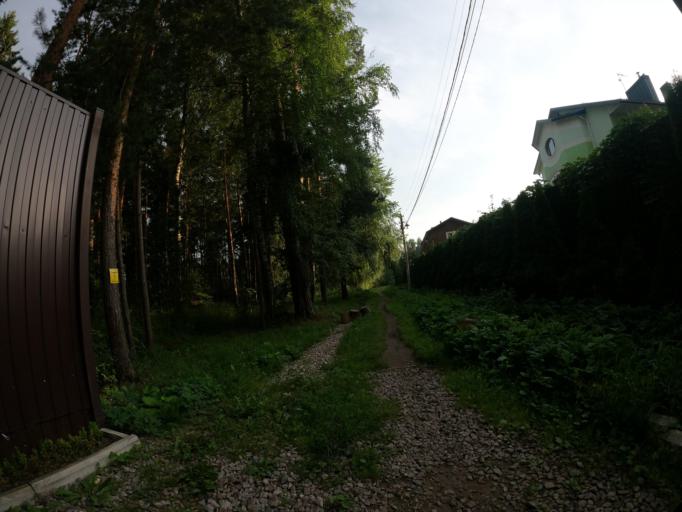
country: RU
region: Moskovskaya
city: Il'inskiy
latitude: 55.6344
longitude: 38.1122
